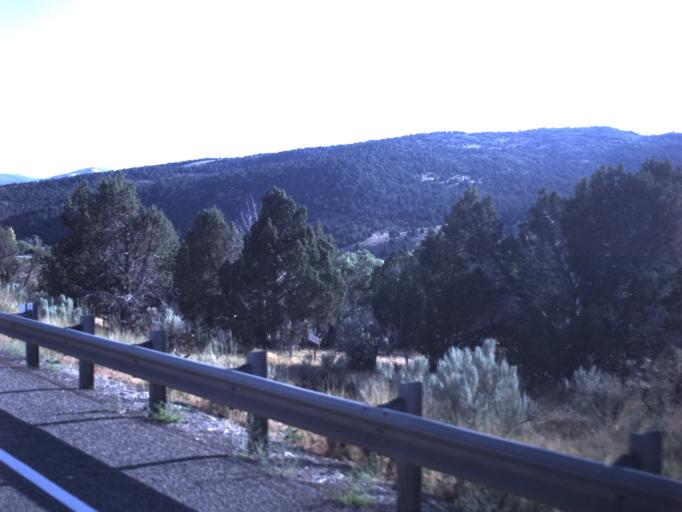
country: US
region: Utah
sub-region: Utah County
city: Woodland Hills
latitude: 39.8997
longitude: -111.5495
